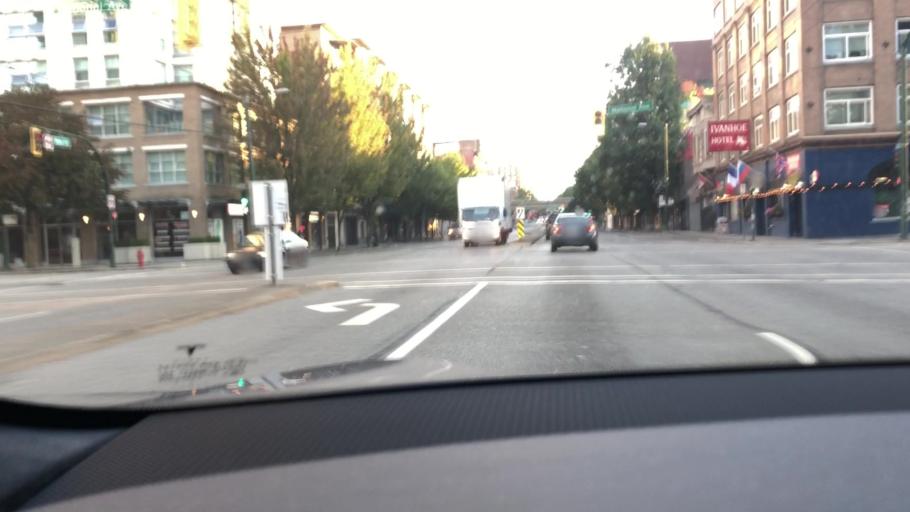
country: CA
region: British Columbia
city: Vancouver
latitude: 49.2747
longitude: -123.0999
